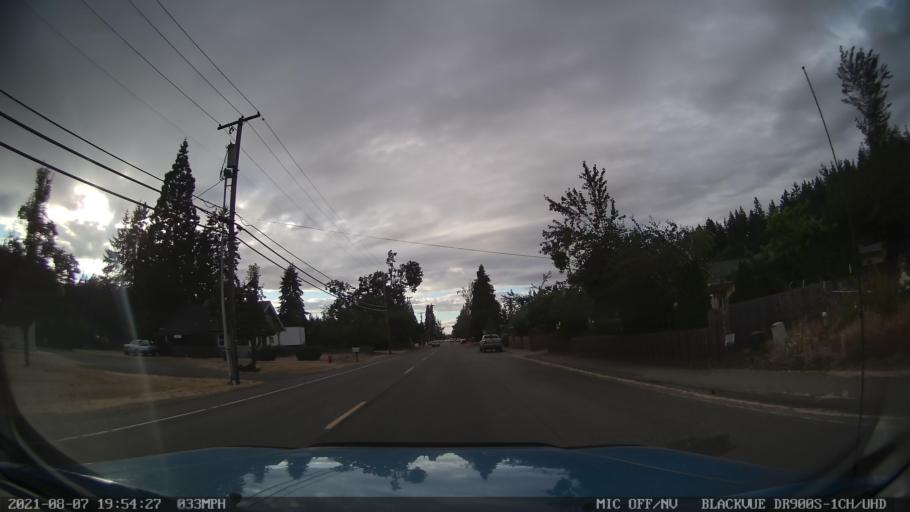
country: US
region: Oregon
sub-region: Marion County
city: Silverton
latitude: 44.9950
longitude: -122.7735
